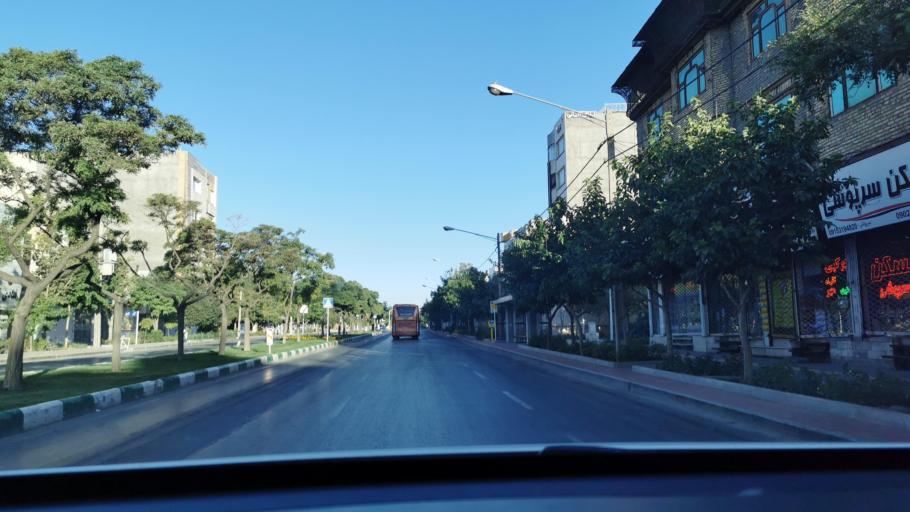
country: IR
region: Razavi Khorasan
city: Mashhad
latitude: 36.3522
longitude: 59.4996
